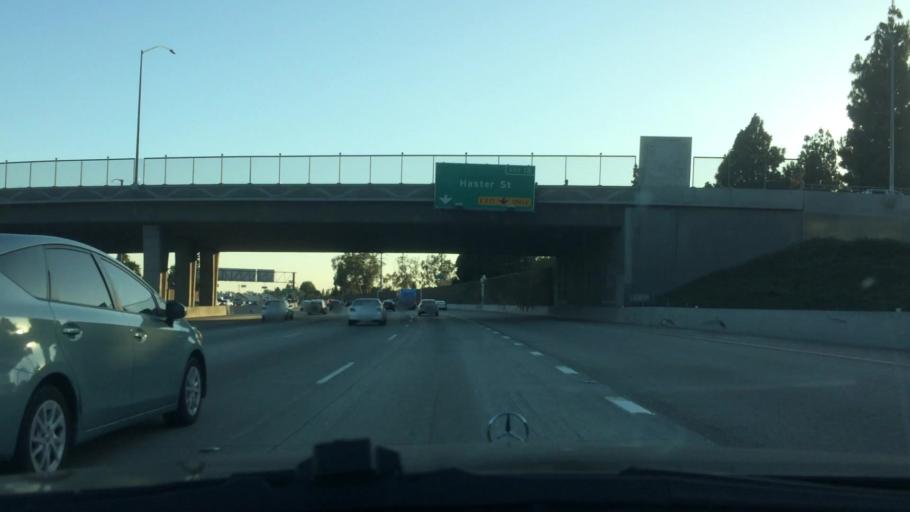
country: US
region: California
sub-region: Orange County
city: Santa Ana
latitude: 33.7789
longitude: -117.8958
